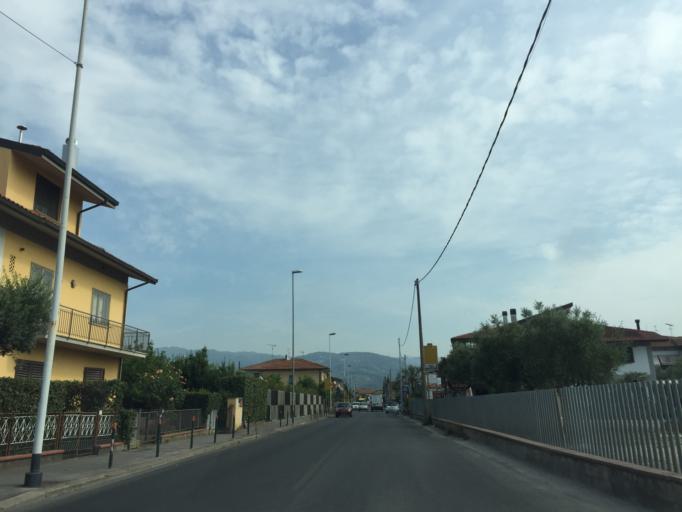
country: IT
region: Tuscany
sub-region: Provincia di Pistoia
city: Margine Coperta-Traversagna
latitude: 43.8634
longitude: 10.7666
